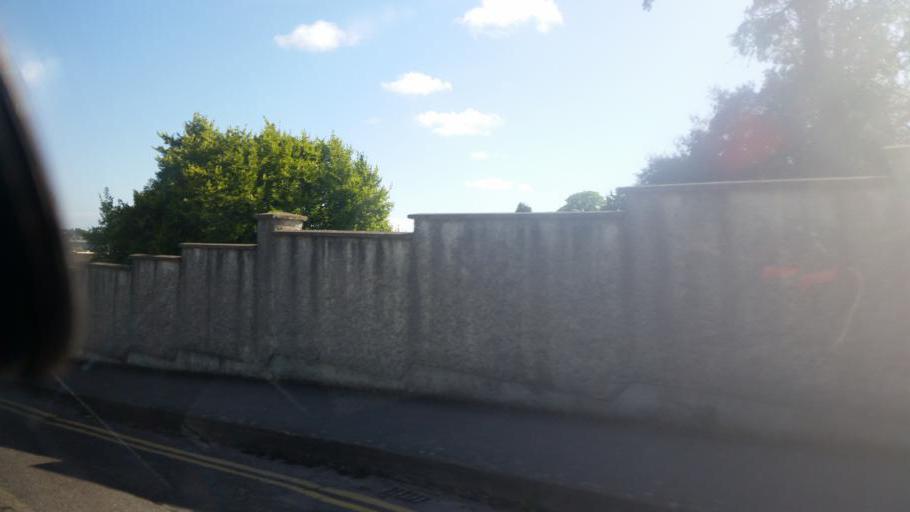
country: IE
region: Munster
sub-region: Waterford
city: Waterford
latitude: 52.2683
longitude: -7.1076
